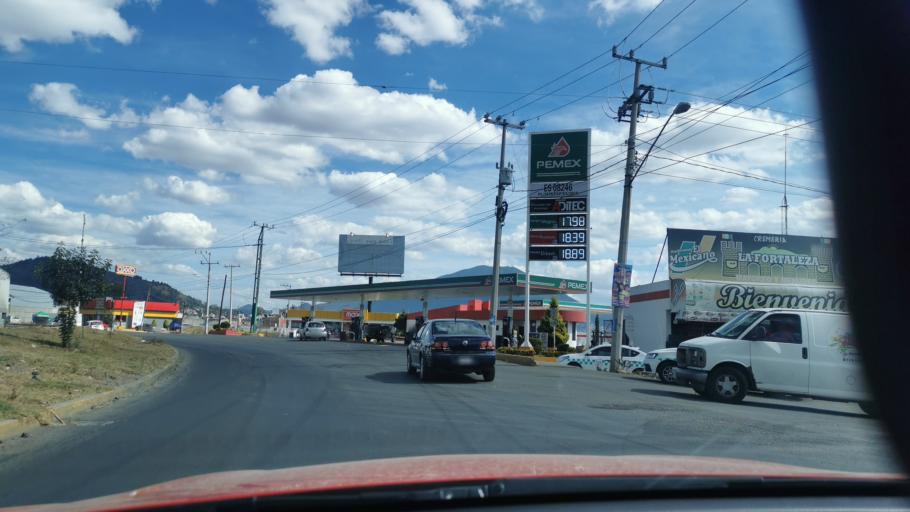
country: MX
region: Mexico
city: Atlacomulco
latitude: 19.7872
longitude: -99.8753
